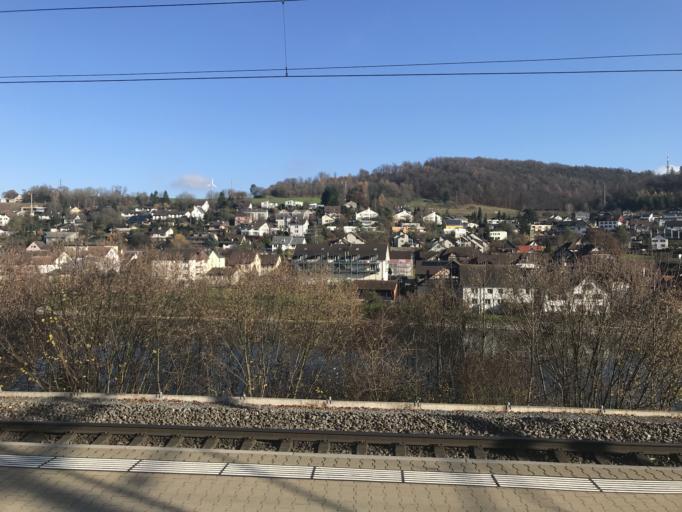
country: CH
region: Zurich
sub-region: Bezirk Andelfingen
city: Flurlingen
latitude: 47.6839
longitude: 8.6250
